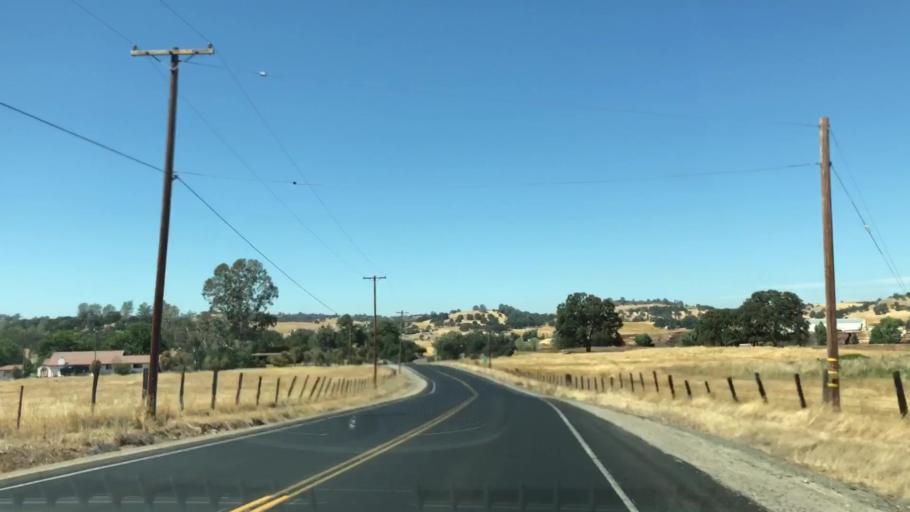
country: US
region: California
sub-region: Tuolumne County
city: Jamestown
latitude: 37.8774
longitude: -120.4441
